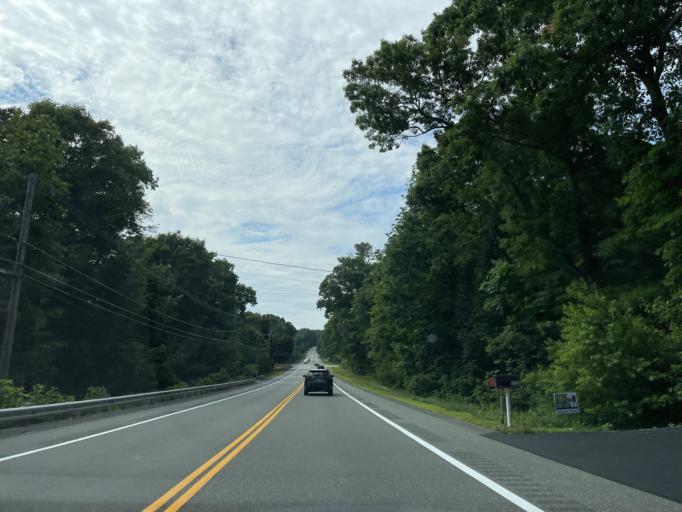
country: US
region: Rhode Island
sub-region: Kent County
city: West Greenwich
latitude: 41.6236
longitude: -71.6775
